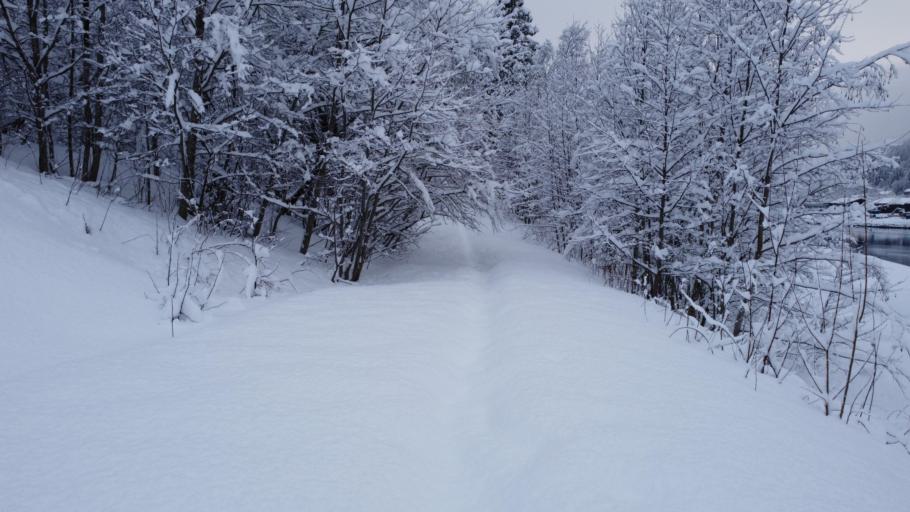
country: NO
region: Nordland
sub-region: Rana
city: Mo i Rana
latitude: 66.3337
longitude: 14.1634
